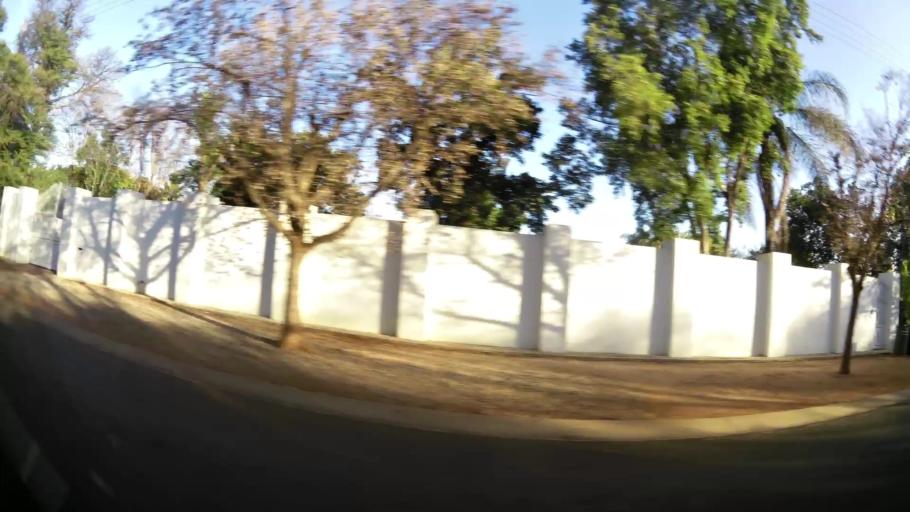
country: ZA
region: Gauteng
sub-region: City of Tshwane Metropolitan Municipality
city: Pretoria
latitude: -25.7041
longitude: 28.2565
